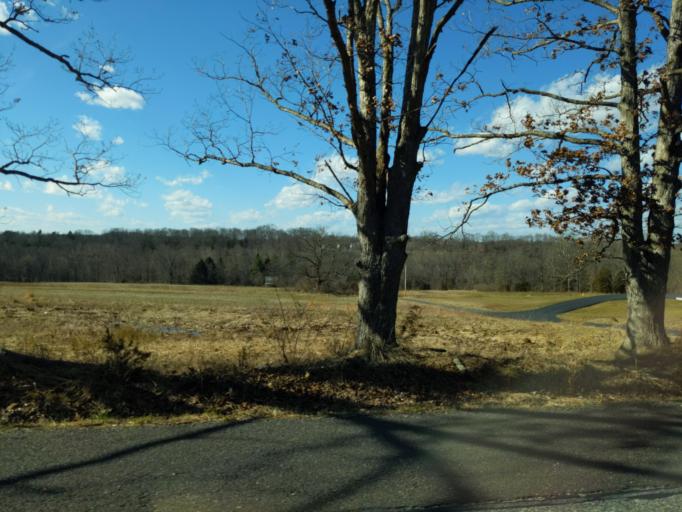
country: US
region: Pennsylvania
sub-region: Montgomery County
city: Red Hill
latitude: 40.3499
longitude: -75.4655
